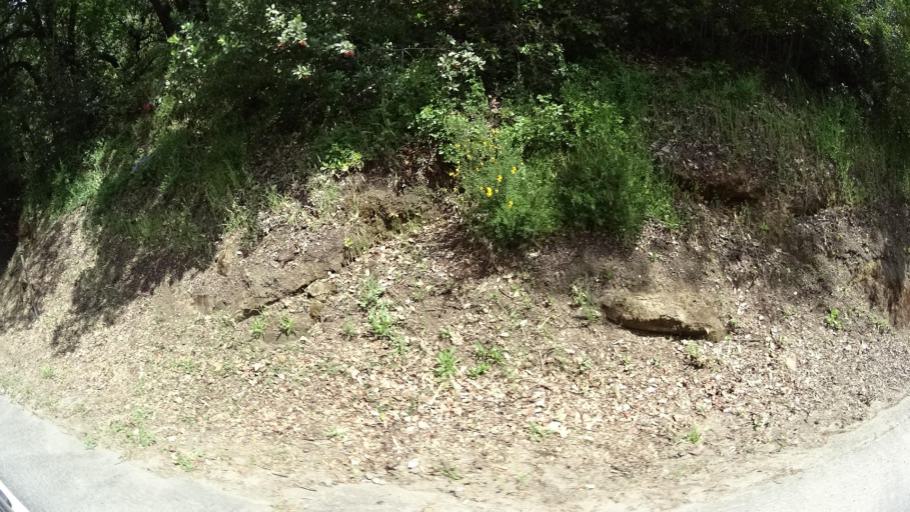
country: US
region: California
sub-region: Humboldt County
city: Redway
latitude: 40.1167
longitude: -123.8178
